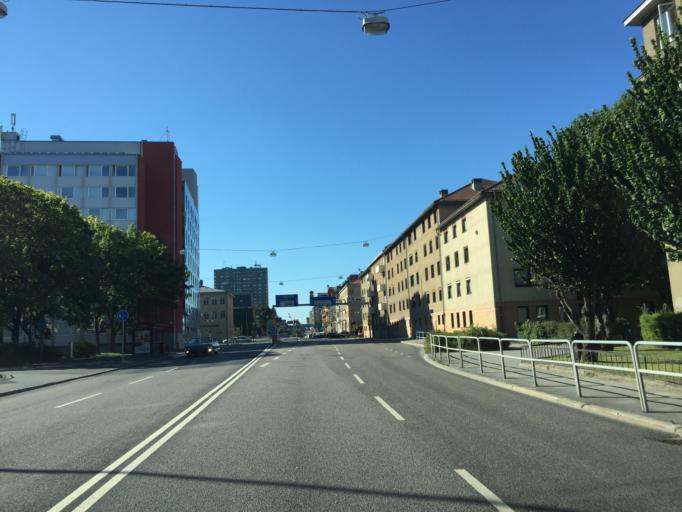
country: SE
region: OErebro
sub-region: Orebro Kommun
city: Orebro
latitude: 59.2678
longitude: 15.2180
